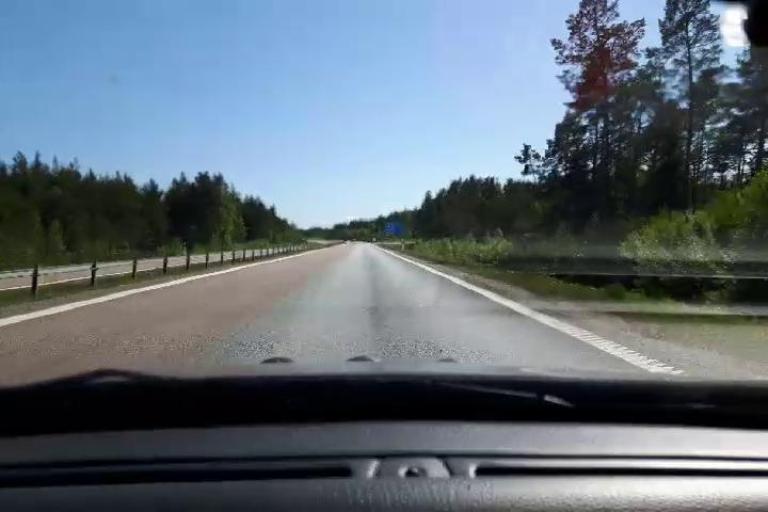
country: SE
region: Gaevleborg
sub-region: Soderhamns Kommun
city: Soderhamn
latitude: 61.3427
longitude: 17.0182
